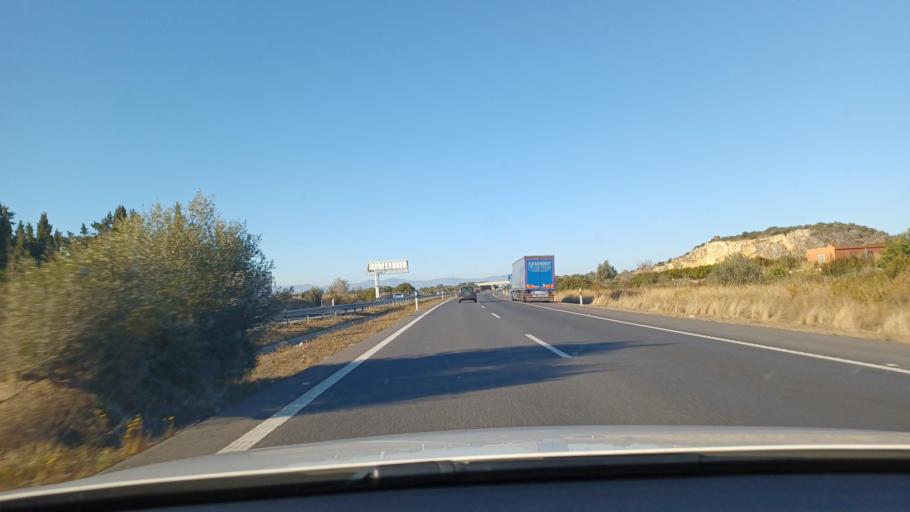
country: ES
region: Valencia
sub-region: Provincia de Castello
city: Vinaros
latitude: 40.4858
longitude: 0.4162
